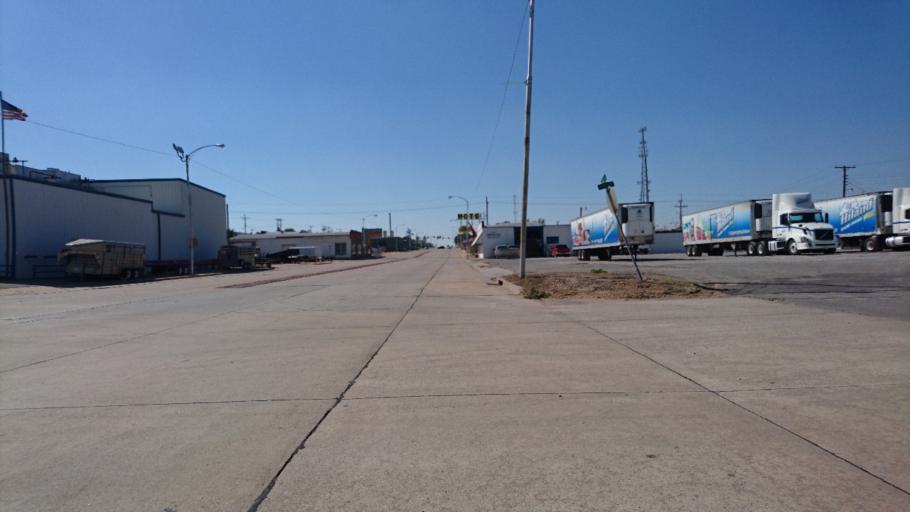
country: US
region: Oklahoma
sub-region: Custer County
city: Clinton
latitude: 35.5155
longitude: -98.9610
